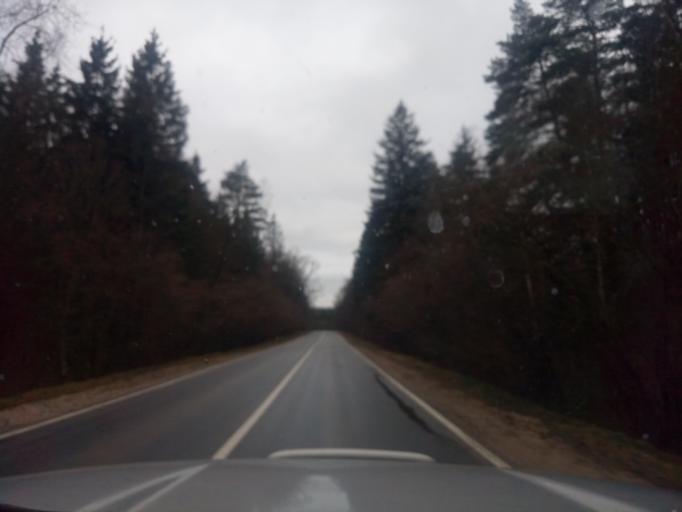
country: BY
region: Minsk
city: Kapyl'
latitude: 53.1634
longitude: 27.1191
